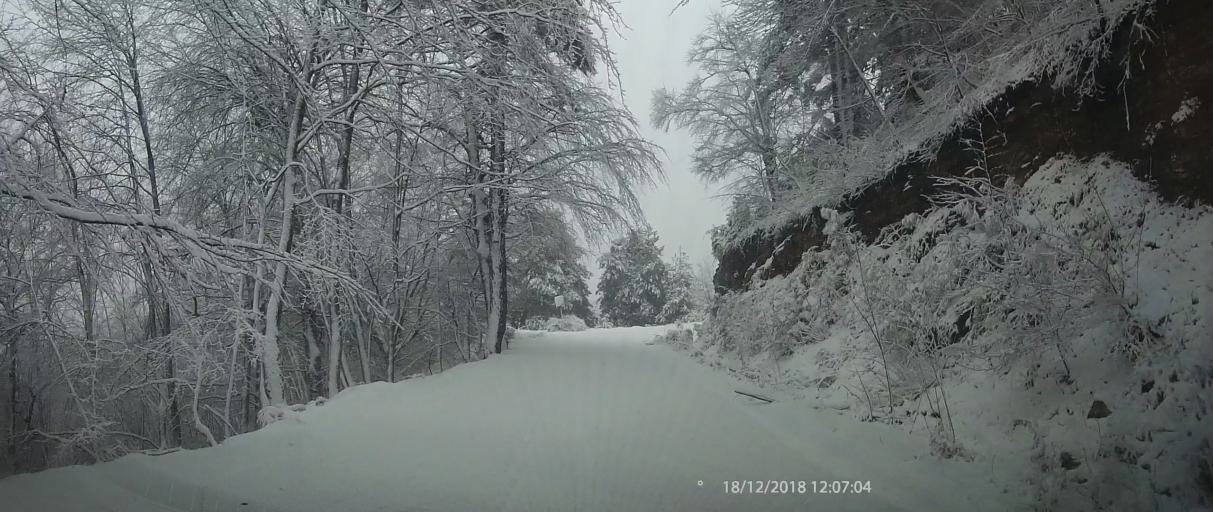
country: GR
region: Central Macedonia
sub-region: Nomos Pierias
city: Litochoro
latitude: 40.1036
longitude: 22.4568
